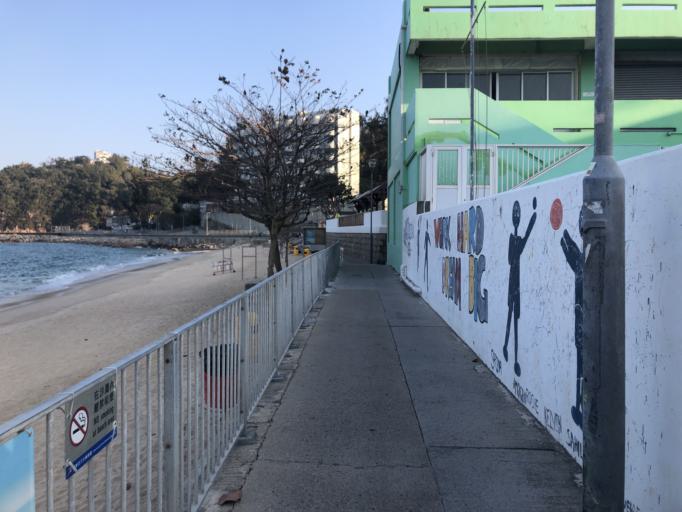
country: HK
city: Yung Shue Wan
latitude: 22.2087
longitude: 114.0312
